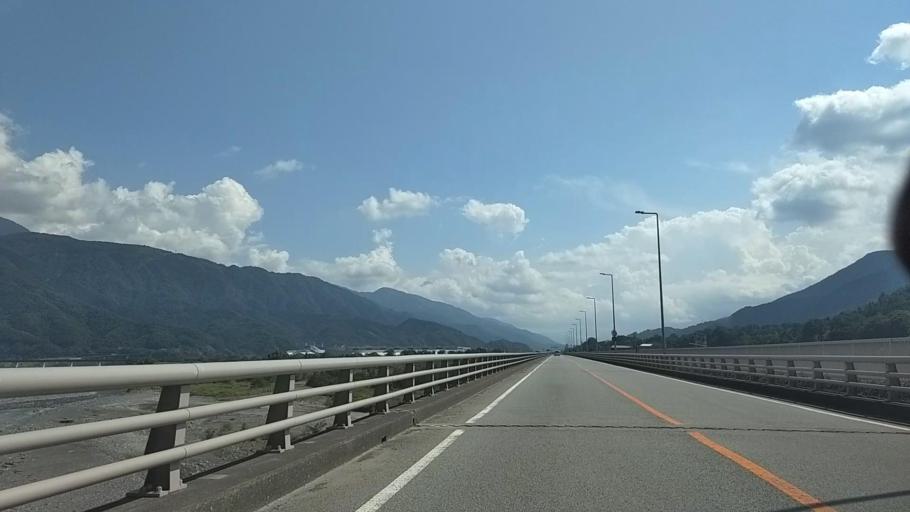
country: JP
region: Yamanashi
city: Ryuo
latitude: 35.4297
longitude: 138.4436
